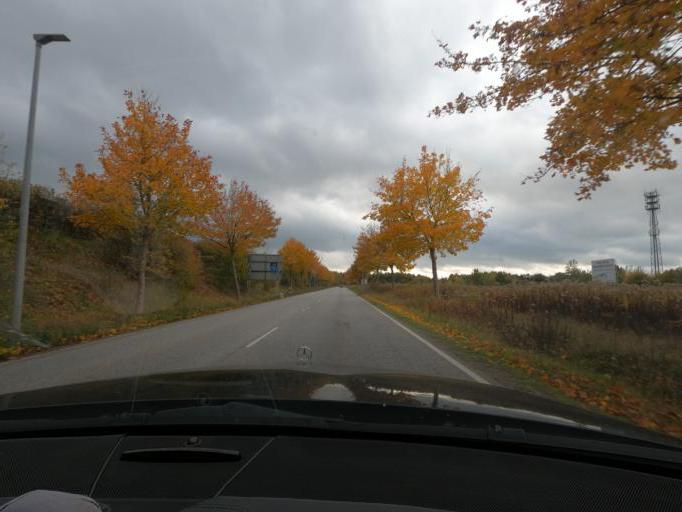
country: DE
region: Schleswig-Holstein
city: Geesthacht
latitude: 53.4544
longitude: 10.3676
